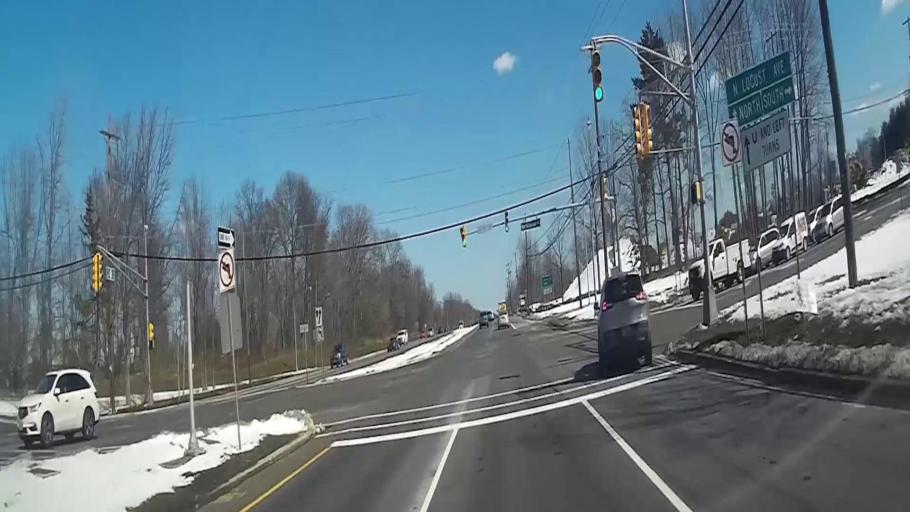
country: US
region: New Jersey
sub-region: Burlington County
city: Marlton
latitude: 39.8938
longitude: -74.9175
